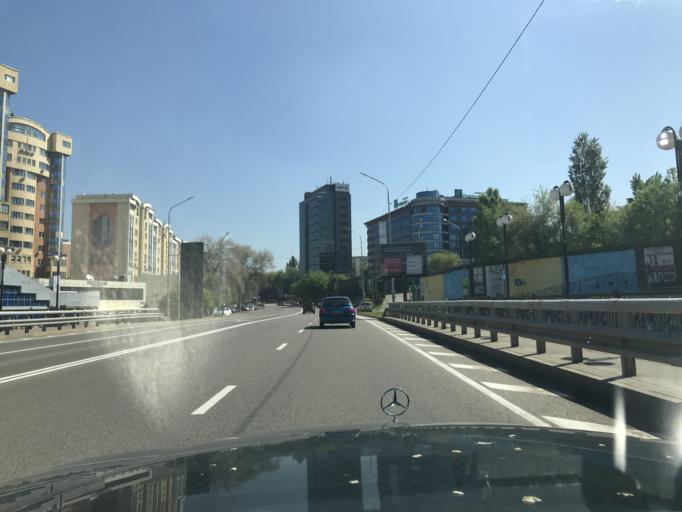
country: KZ
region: Almaty Qalasy
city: Almaty
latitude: 43.2326
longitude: 76.9368
